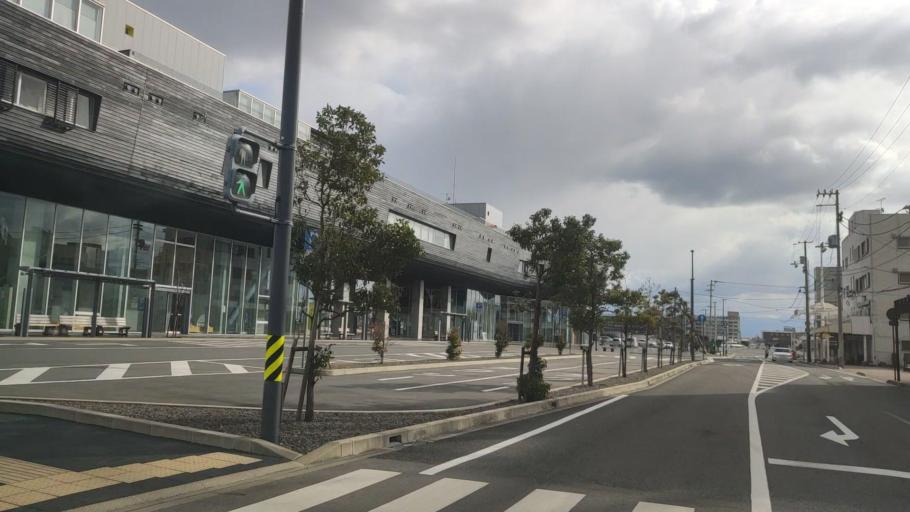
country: JP
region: Ehime
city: Saijo
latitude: 34.0700
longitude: 133.0044
